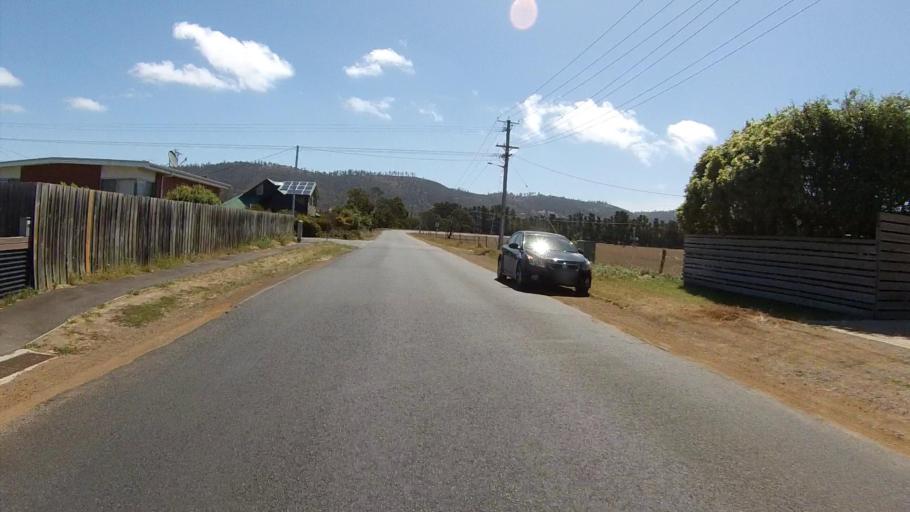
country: AU
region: Tasmania
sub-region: Clarence
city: Acton Park
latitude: -42.8938
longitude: 147.4971
